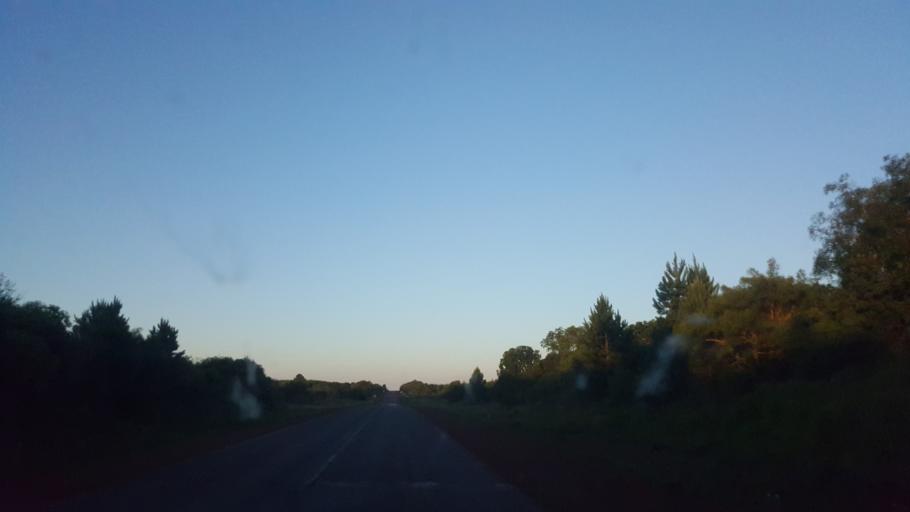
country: AR
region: Corrientes
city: Santo Tome
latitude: -28.4116
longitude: -55.9829
